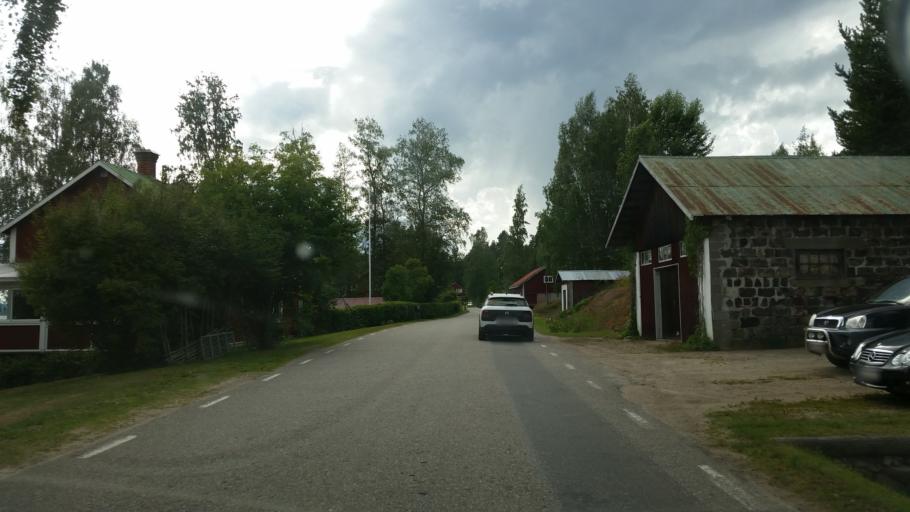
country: SE
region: Gaevleborg
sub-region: Hudiksvalls Kommun
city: Delsbo
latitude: 61.9209
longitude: 16.6108
